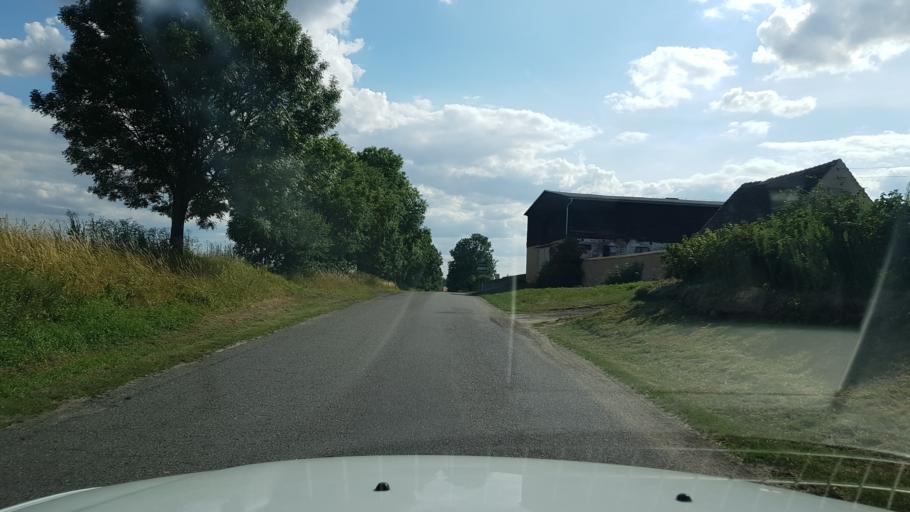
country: PL
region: West Pomeranian Voivodeship
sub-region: Powiat gryfinski
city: Stare Czarnowo
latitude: 53.3023
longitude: 14.8091
